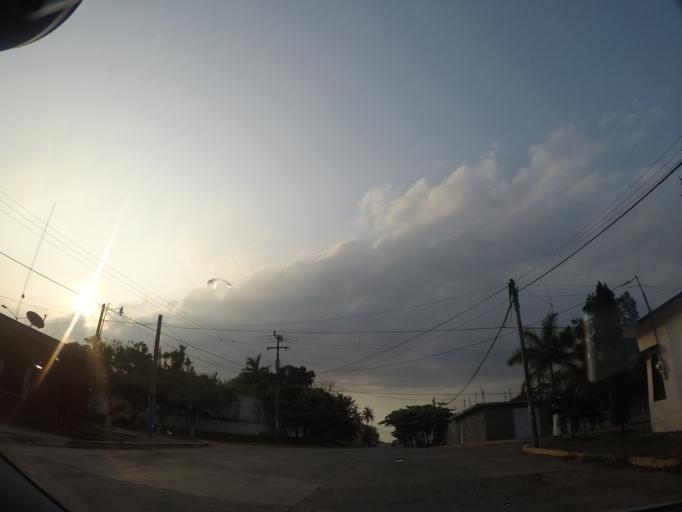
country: MX
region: Oaxaca
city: Matias Romero
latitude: 16.8730
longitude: -95.0430
